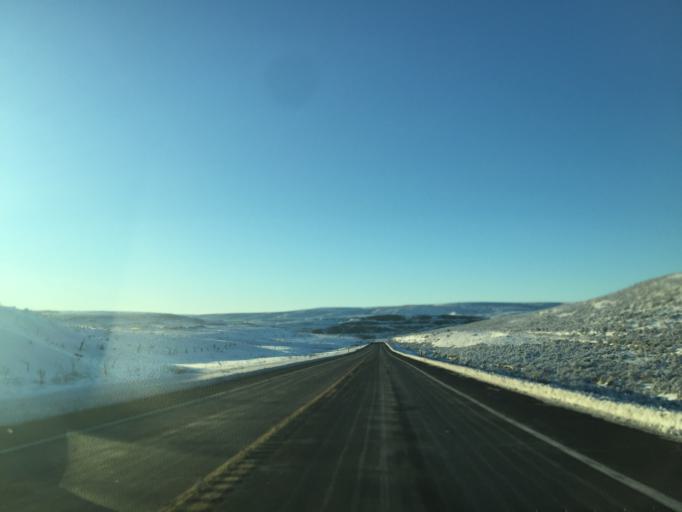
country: US
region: Washington
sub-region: Grant County
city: Soap Lake
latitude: 47.6068
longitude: -119.6477
